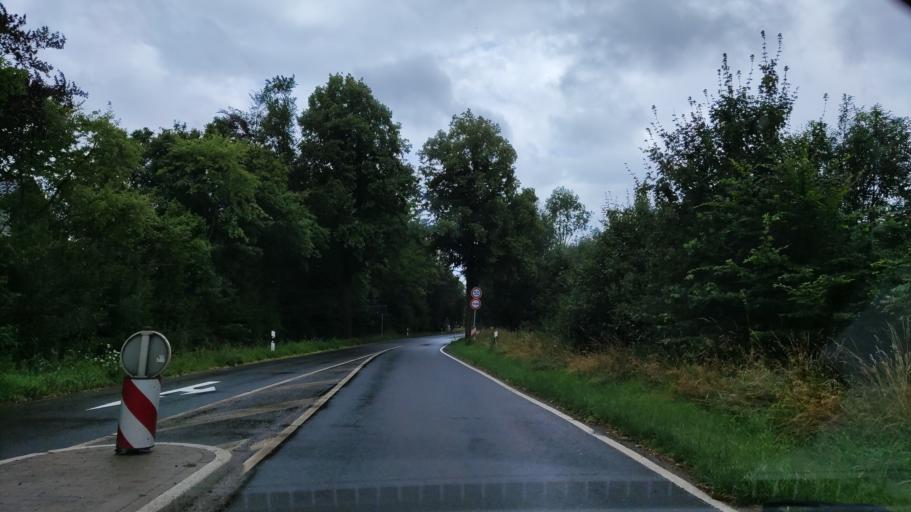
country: DE
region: North Rhine-Westphalia
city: Sendenhorst
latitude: 51.8376
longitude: 7.8259
